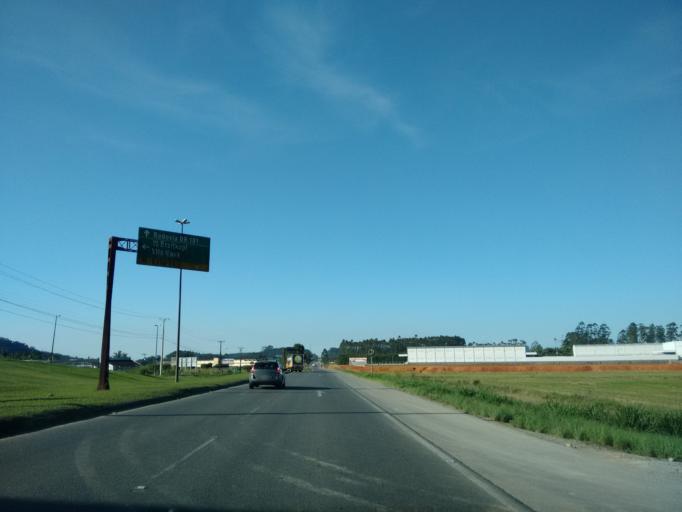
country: BR
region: Santa Catarina
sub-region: Guaramirim
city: Guaramirim
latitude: -26.4675
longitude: -48.9610
